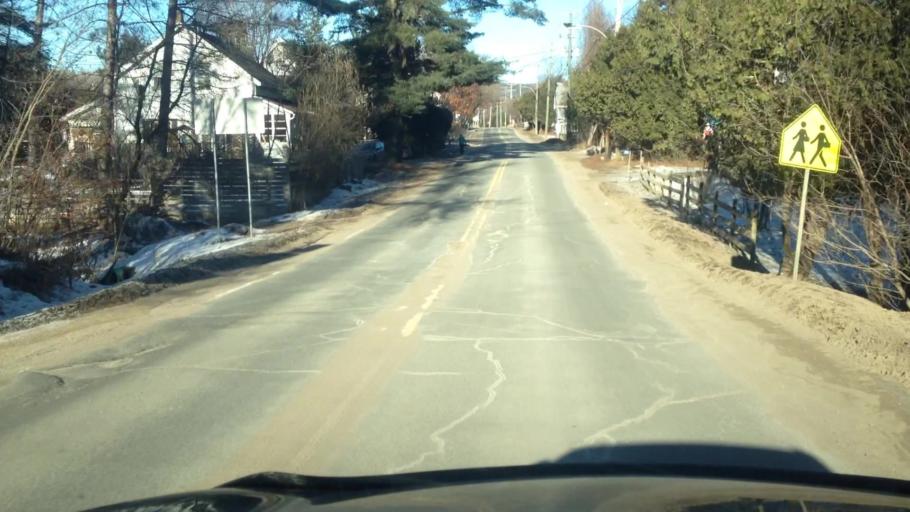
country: CA
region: Quebec
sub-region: Laurentides
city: Mont-Tremblant
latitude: 45.9680
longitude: -74.6160
